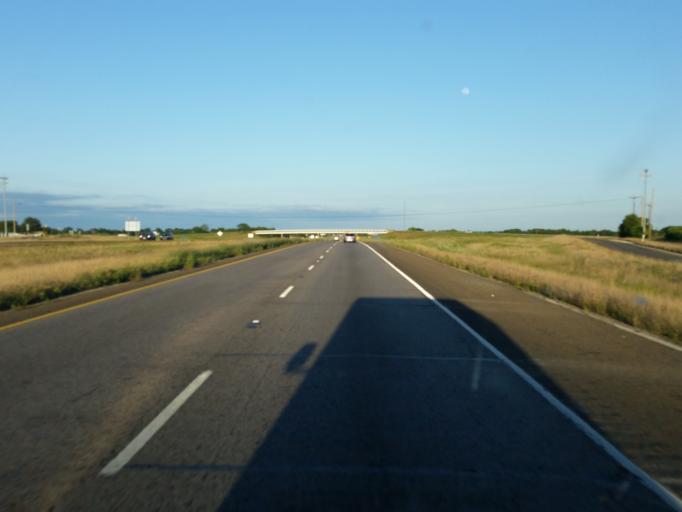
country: US
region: Texas
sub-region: Van Zandt County
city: Wills Point
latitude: 32.6565
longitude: -96.0992
